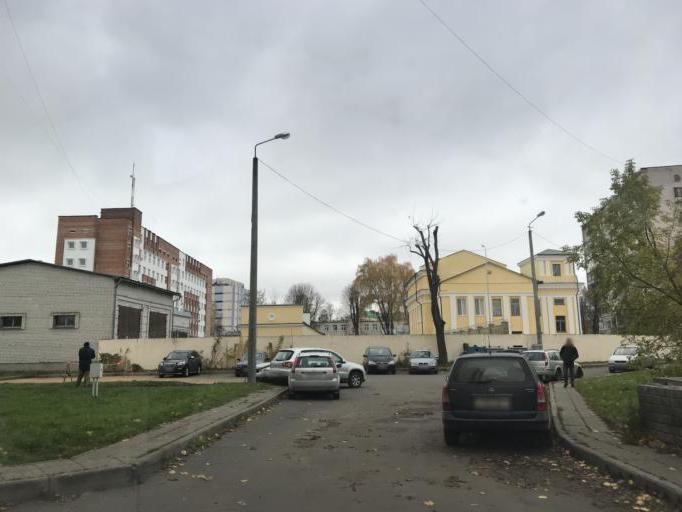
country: BY
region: Mogilev
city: Mahilyow
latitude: 53.9003
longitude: 30.3478
